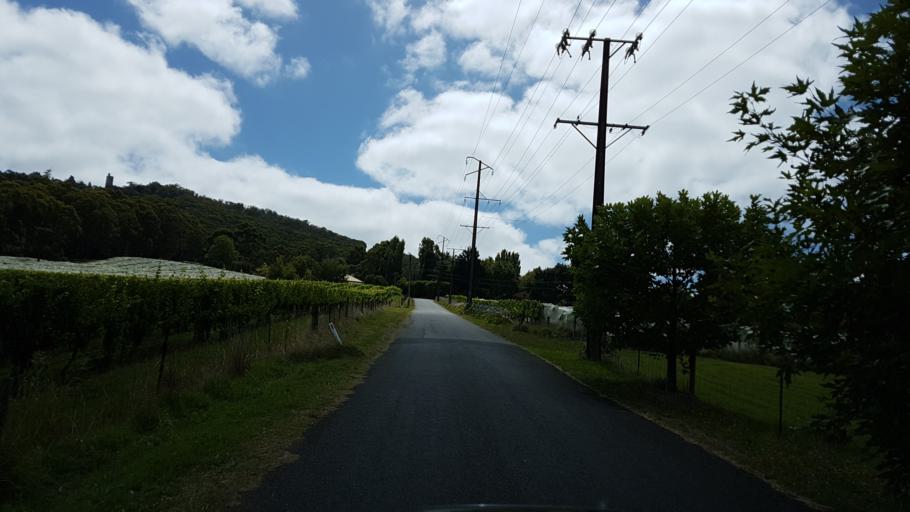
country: AU
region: South Australia
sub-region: Adelaide Hills
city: Crafers
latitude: -34.9810
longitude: 138.7202
